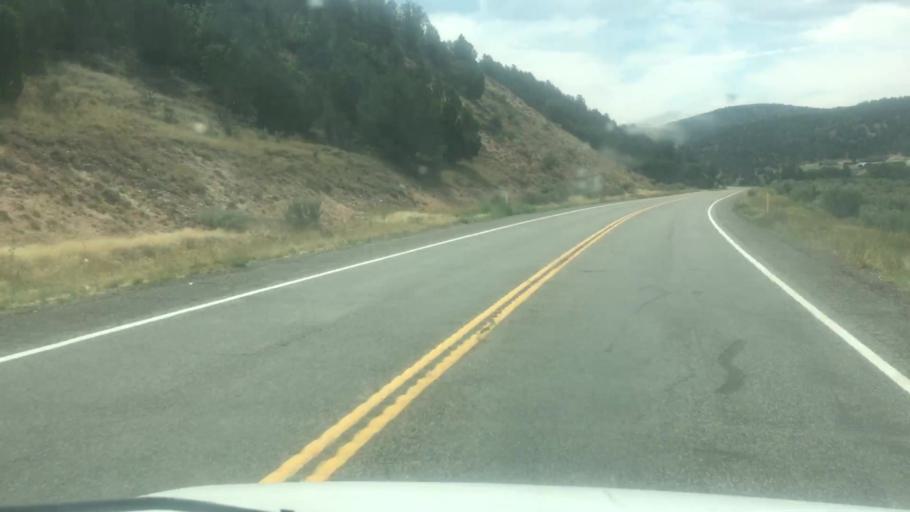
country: US
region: Utah
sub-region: Utah County
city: Woodland Hills
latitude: 39.9196
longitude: -111.5455
